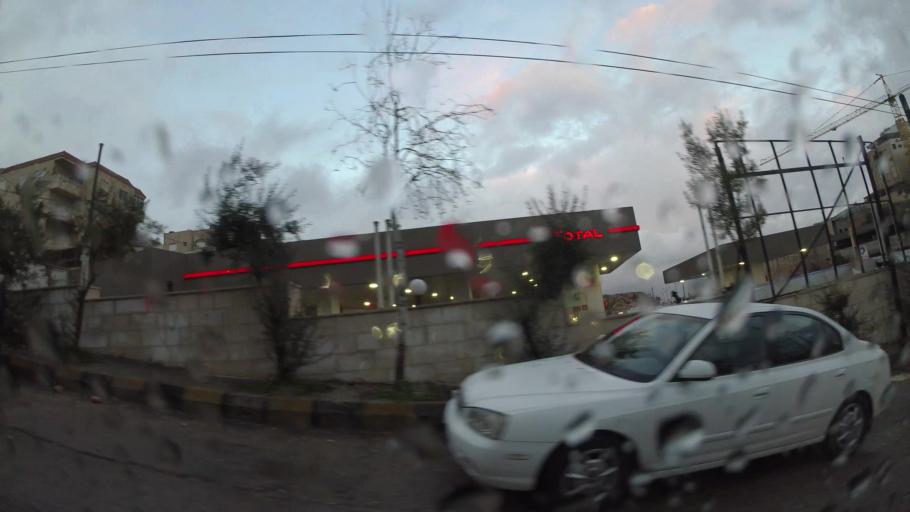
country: JO
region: Amman
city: Amman
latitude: 31.9942
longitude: 35.9211
